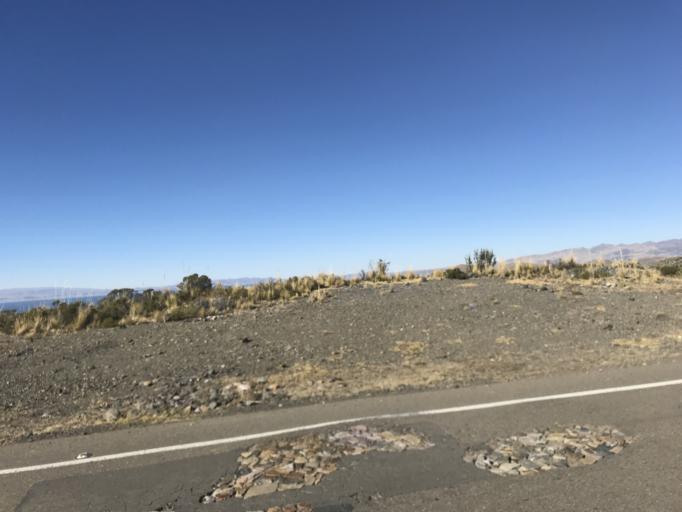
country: PE
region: Puno
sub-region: Yunguyo
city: Yunguyo
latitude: -16.1633
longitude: -68.9885
